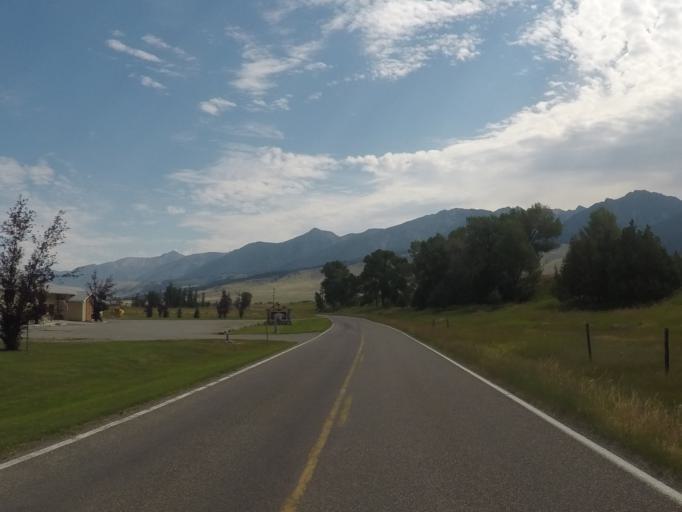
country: US
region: Montana
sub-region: Park County
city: Livingston
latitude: 45.4203
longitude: -110.6321
